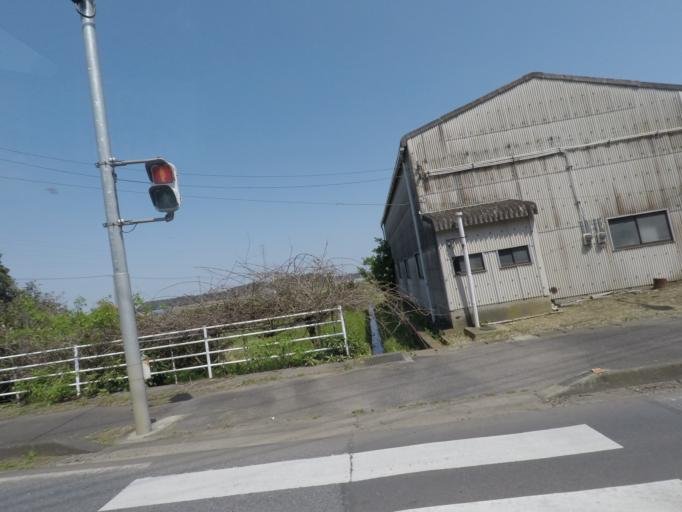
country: JP
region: Chiba
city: Yokaichiba
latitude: 35.6775
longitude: 140.4667
